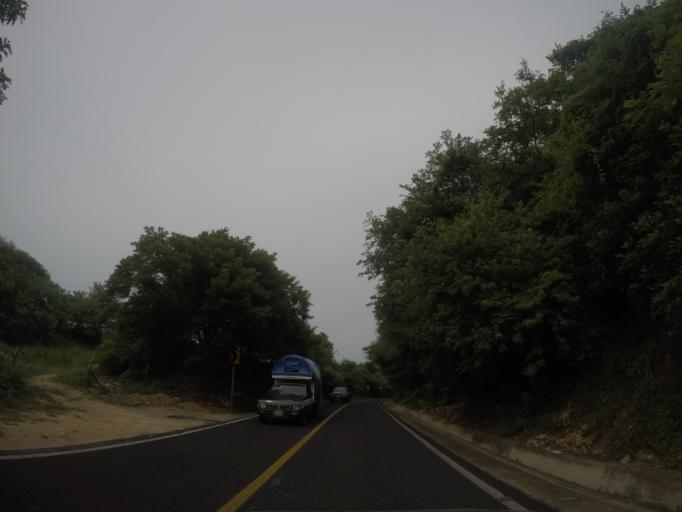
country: MX
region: Oaxaca
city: San Pedro Mixtepec
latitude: 15.9507
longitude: -97.2574
